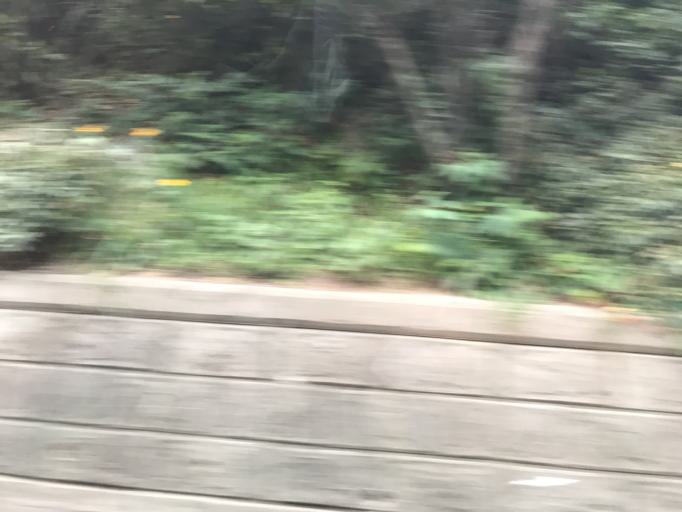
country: KR
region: Seoul
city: Seoul
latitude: 37.5659
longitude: 126.9449
